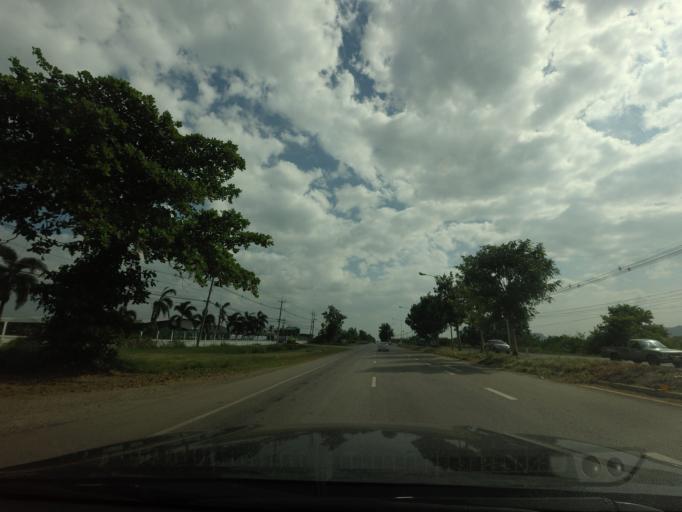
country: TH
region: Lop Buri
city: Chai Badan
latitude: 15.2556
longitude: 101.1253
